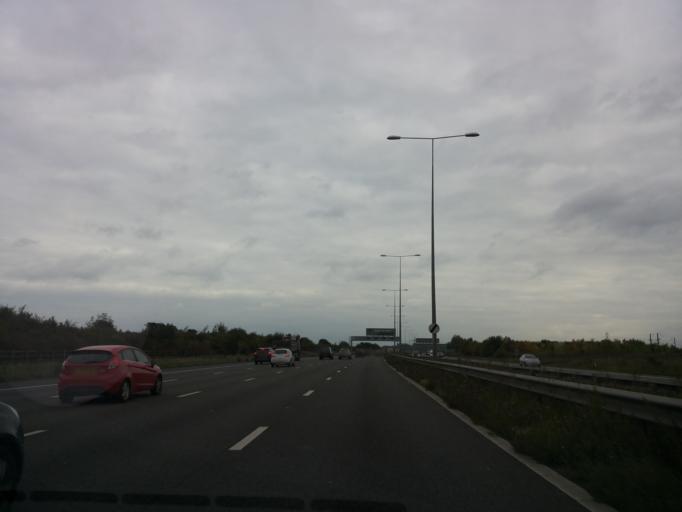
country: GB
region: England
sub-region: Kent
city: Gravesend
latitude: 51.4129
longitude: 0.3683
